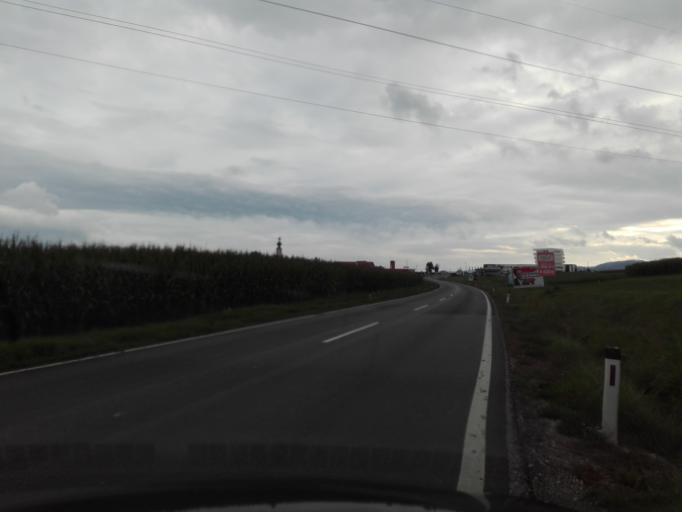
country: AT
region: Upper Austria
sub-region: Politischer Bezirk Vocklabruck
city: Wolfsegg am Hausruck
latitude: 48.2112
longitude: 13.6826
